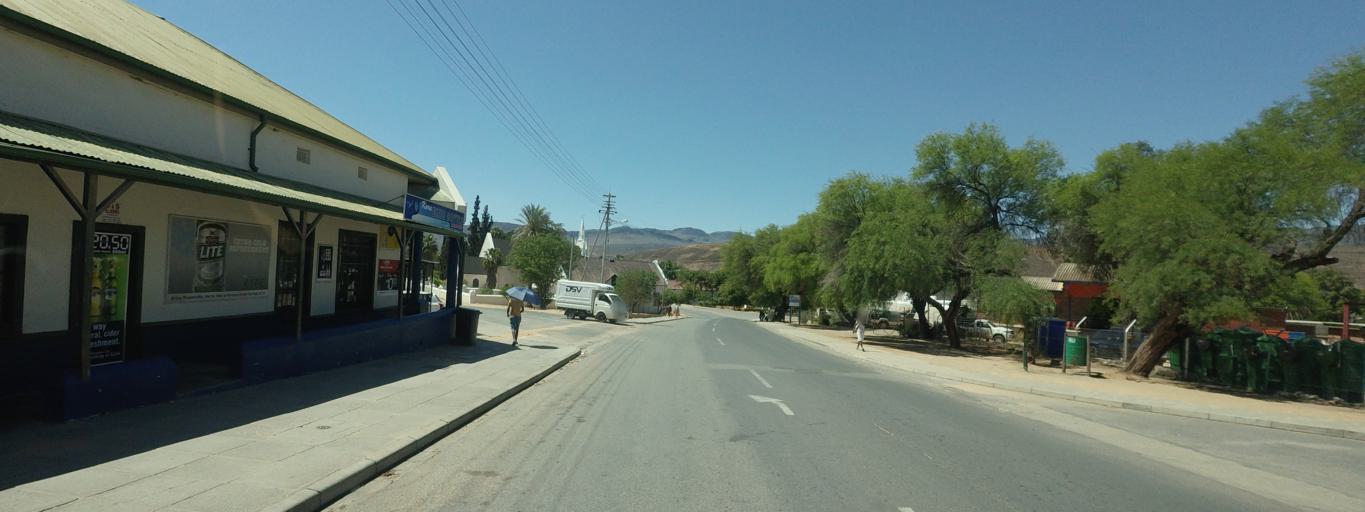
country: ZA
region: Western Cape
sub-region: West Coast District Municipality
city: Clanwilliam
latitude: -32.1817
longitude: 18.8932
